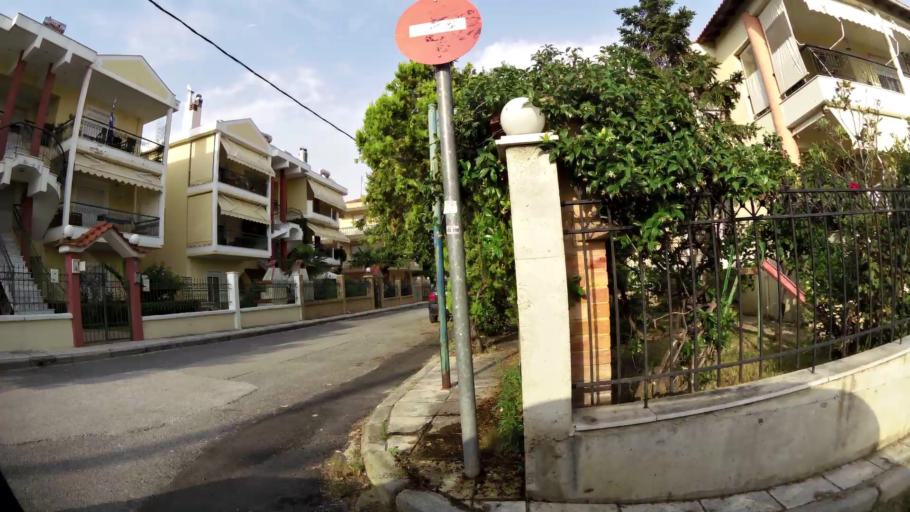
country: GR
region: Central Macedonia
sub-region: Nomos Thessalonikis
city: Oraiokastro
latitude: 40.7218
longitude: 22.9023
